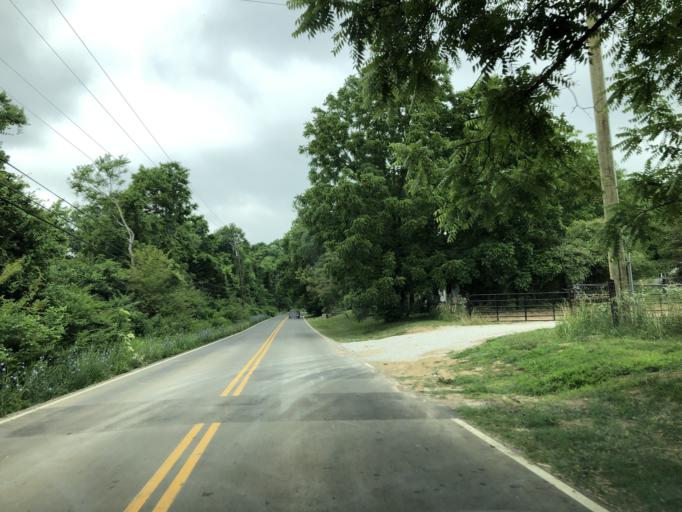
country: US
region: Tennessee
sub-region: Davidson County
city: Goodlettsville
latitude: 36.2935
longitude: -86.7432
